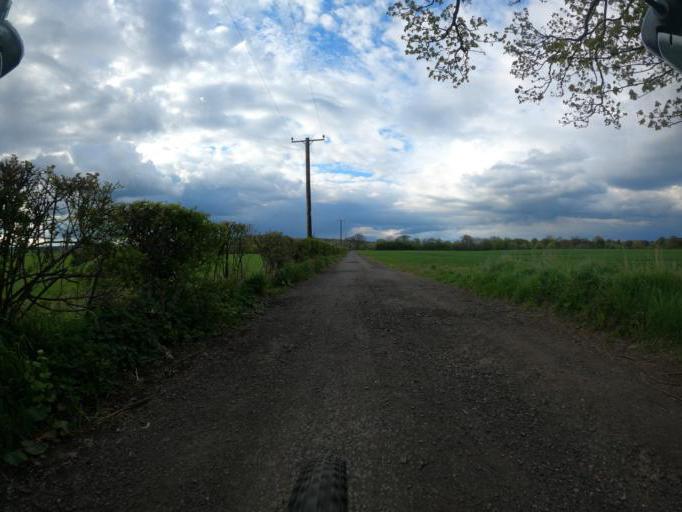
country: GB
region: Scotland
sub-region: Edinburgh
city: Ratho
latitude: 55.9587
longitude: -3.3390
